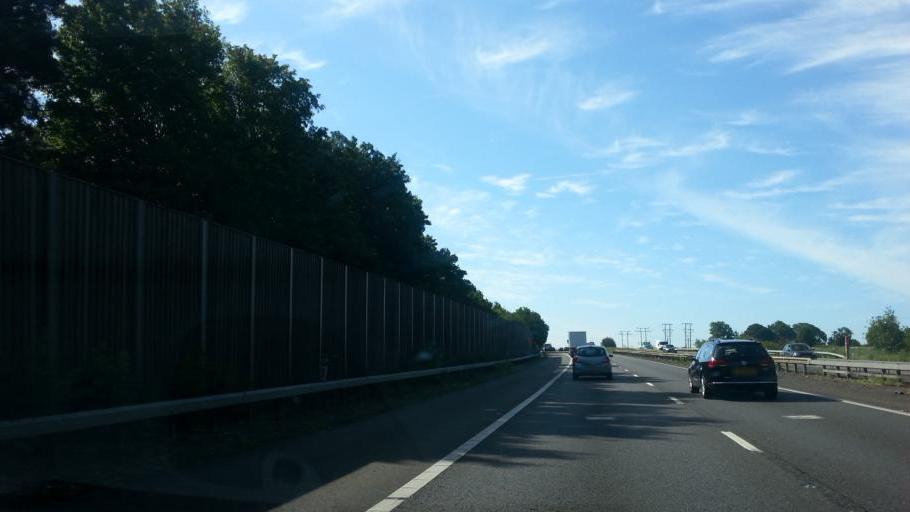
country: GB
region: England
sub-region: Hertfordshire
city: Stevenage
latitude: 51.9073
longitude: -0.2264
